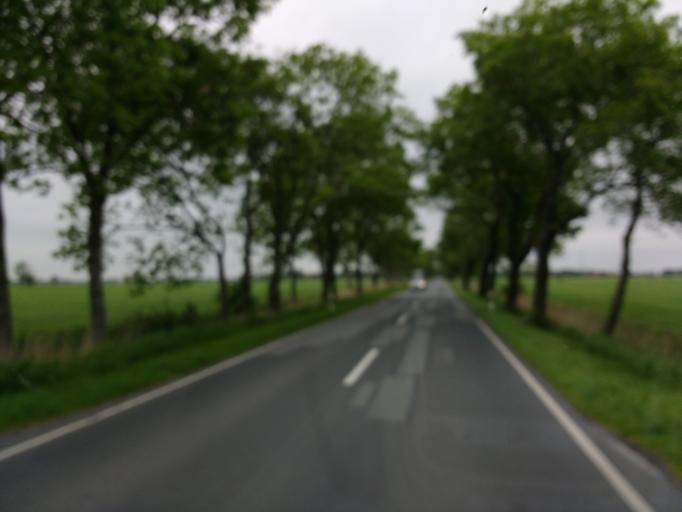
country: DE
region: Lower Saxony
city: Jever
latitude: 53.6189
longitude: 7.9312
